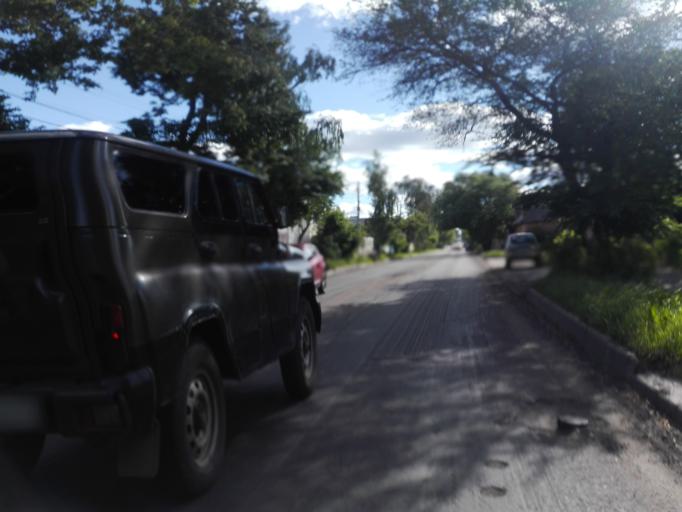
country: RU
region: Orjol
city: Orel
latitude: 52.9545
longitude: 36.0489
